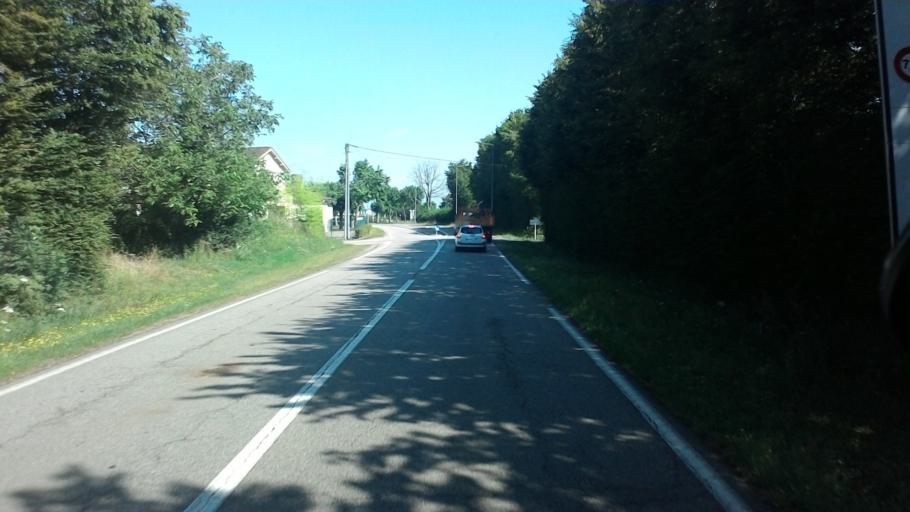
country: FR
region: Rhone-Alpes
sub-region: Departement de l'Ain
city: Saint-Trivier-de-Courtes
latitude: 46.4583
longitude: 5.0846
